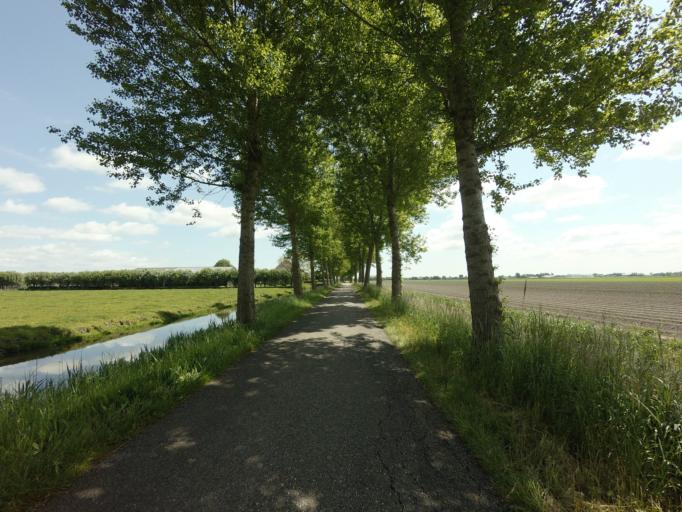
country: NL
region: North Holland
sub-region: Gemeente Beemster
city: Halfweg
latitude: 52.5995
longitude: 4.9246
